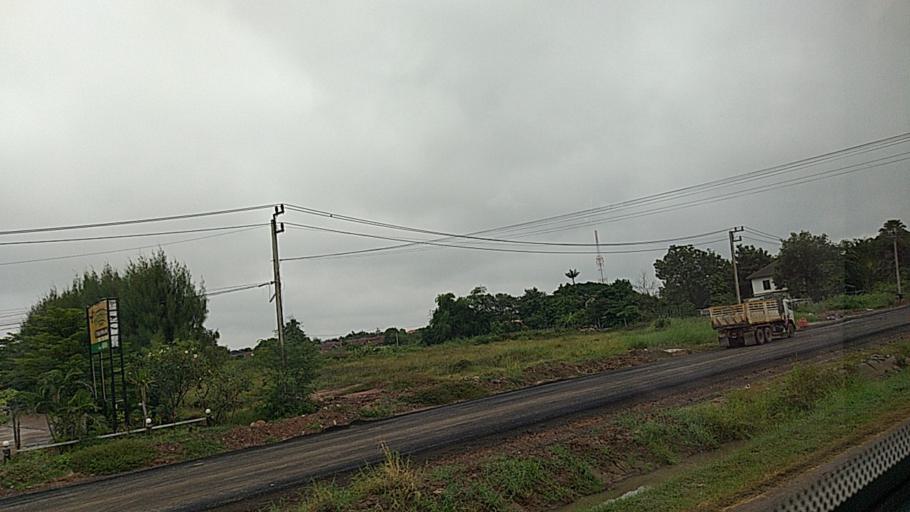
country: TH
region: Nakhon Ratchasima
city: Nakhon Ratchasima
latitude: 14.9951
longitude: 102.0857
